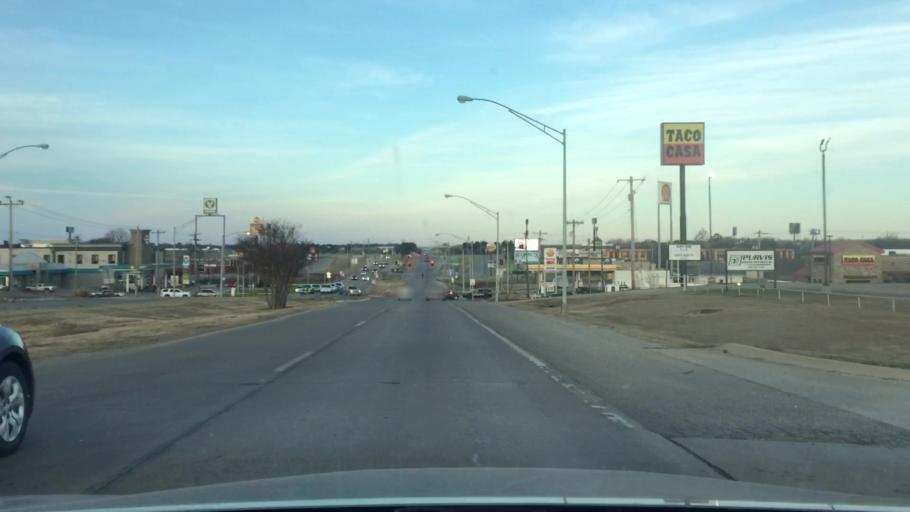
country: US
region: Oklahoma
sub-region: Carter County
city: Ardmore
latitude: 34.1730
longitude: -97.1588
